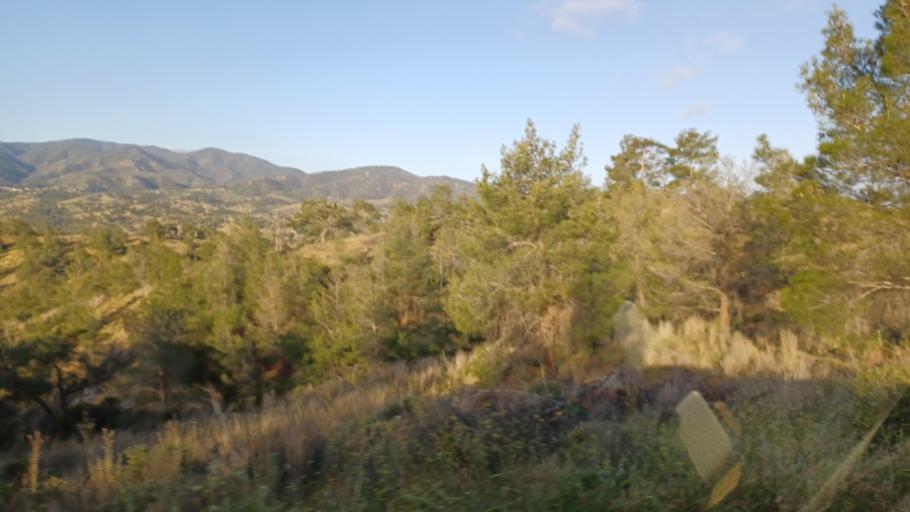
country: CY
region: Lefkosia
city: Peristerona
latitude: 35.0651
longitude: 33.0395
